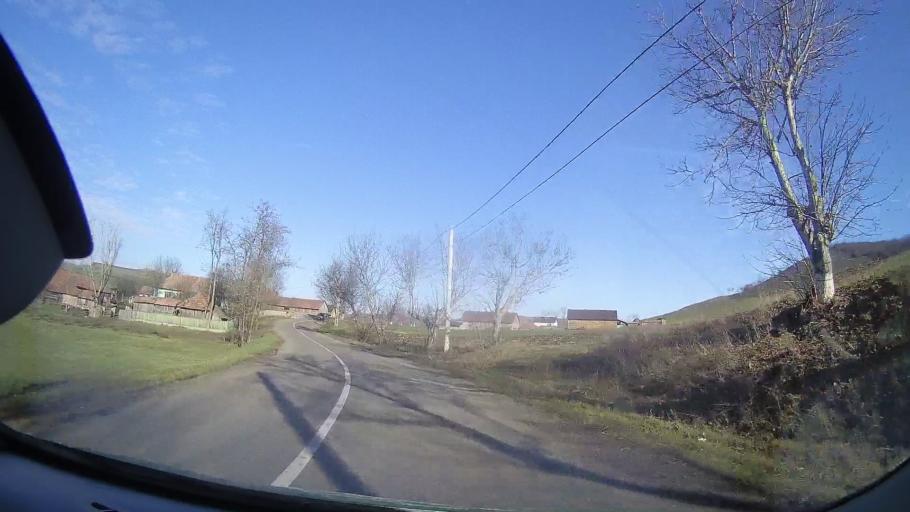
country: RO
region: Mures
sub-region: Comuna Band
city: Band
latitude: 46.5733
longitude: 24.3478
